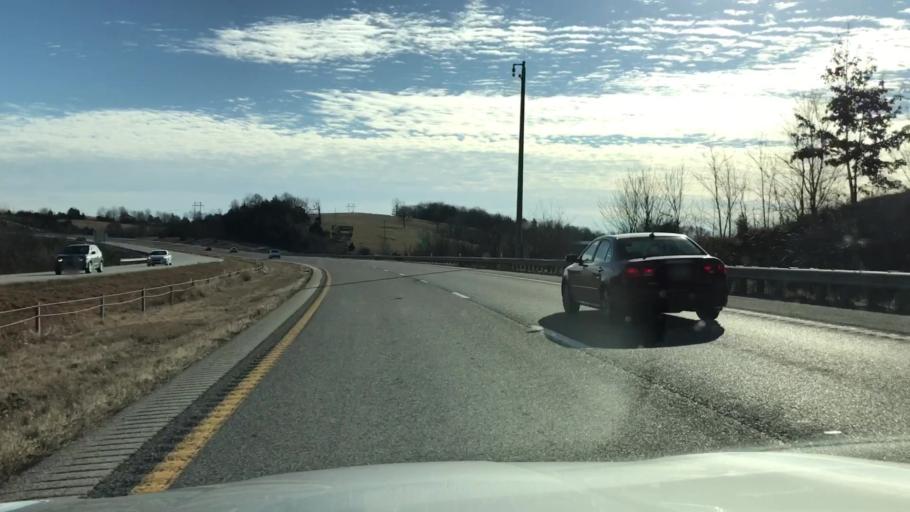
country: US
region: Missouri
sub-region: Cooper County
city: Boonville
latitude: 38.9349
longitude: -92.9784
